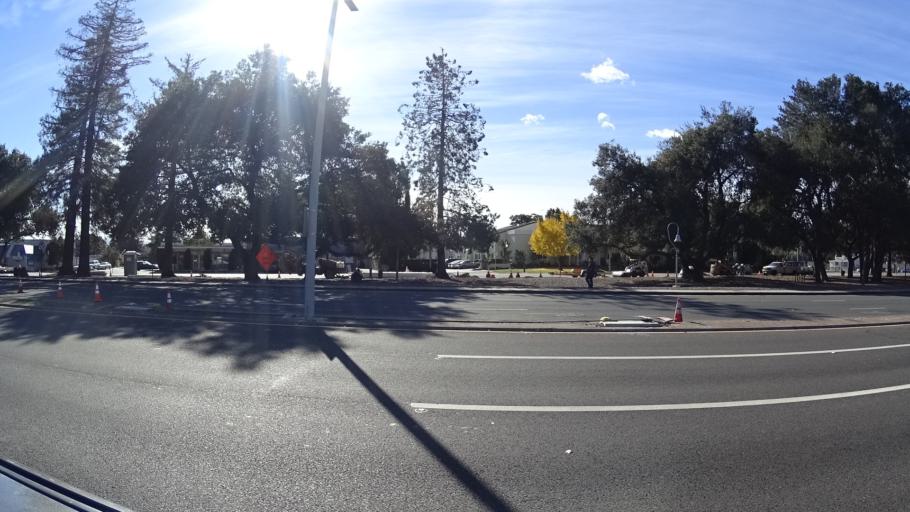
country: US
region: California
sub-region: Santa Clara County
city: Sunnyvale
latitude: 37.3527
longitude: -122.0129
